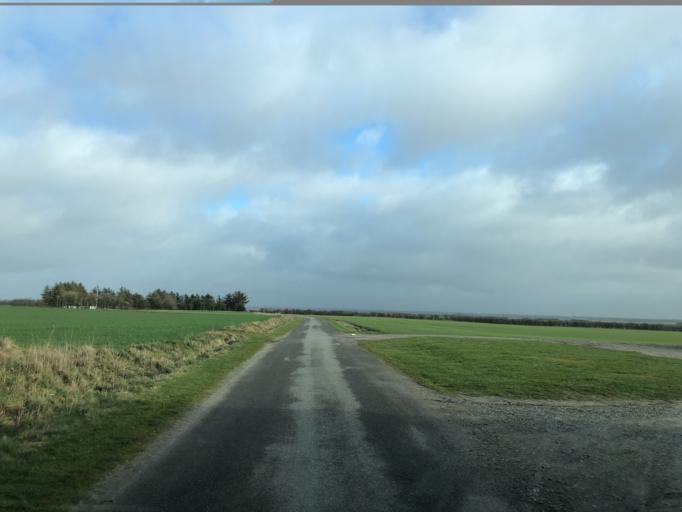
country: DK
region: Central Jutland
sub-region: Holstebro Kommune
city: Ulfborg
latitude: 56.3106
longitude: 8.2191
